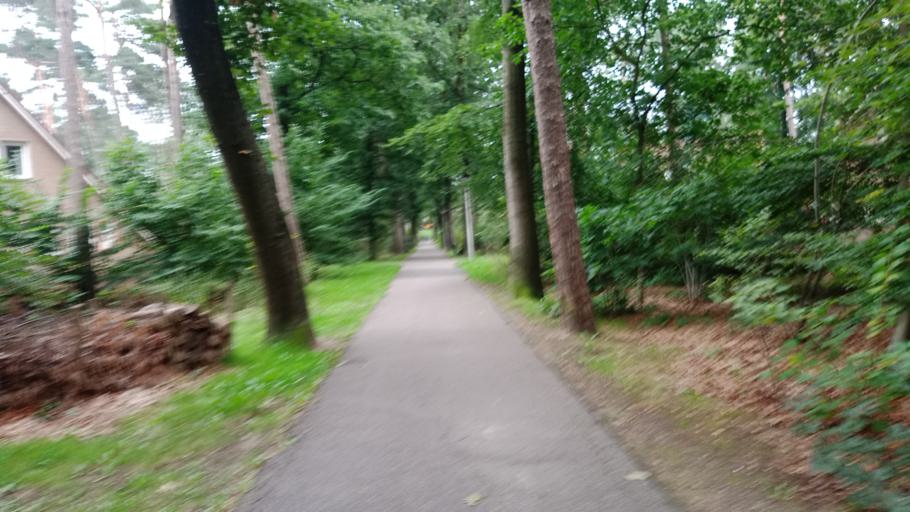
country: NL
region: Gelderland
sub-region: Gemeente Oldebroek
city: Oldebroek
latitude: 52.4406
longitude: 5.9518
